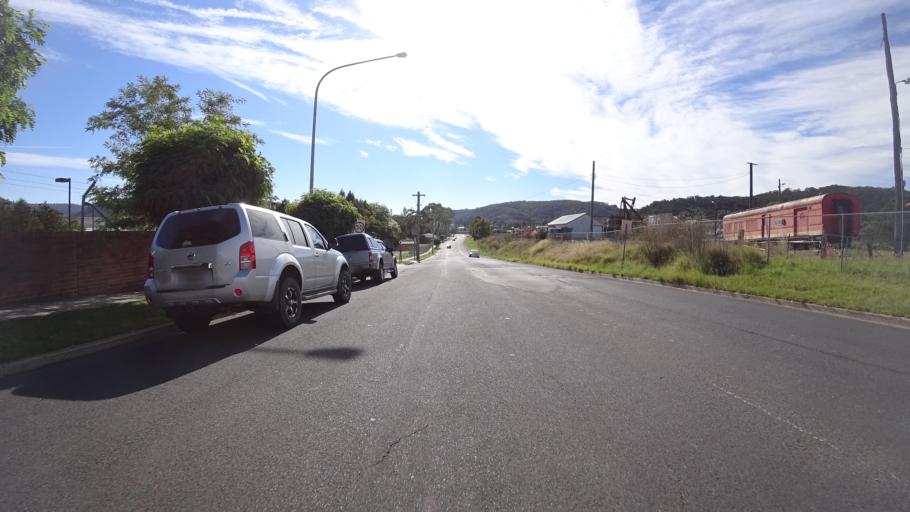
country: AU
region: New South Wales
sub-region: Lithgow
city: Lithgow
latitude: -33.4788
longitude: 150.1621
